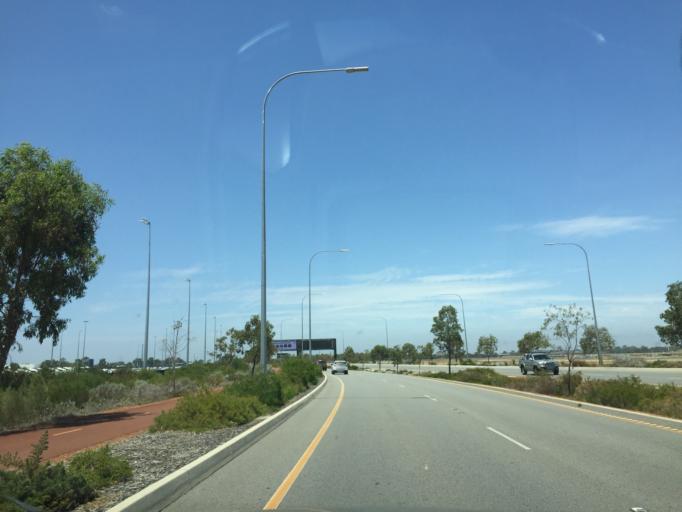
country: AU
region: Western Australia
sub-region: Belmont
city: Redcliffe
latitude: -31.9501
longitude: 115.9708
